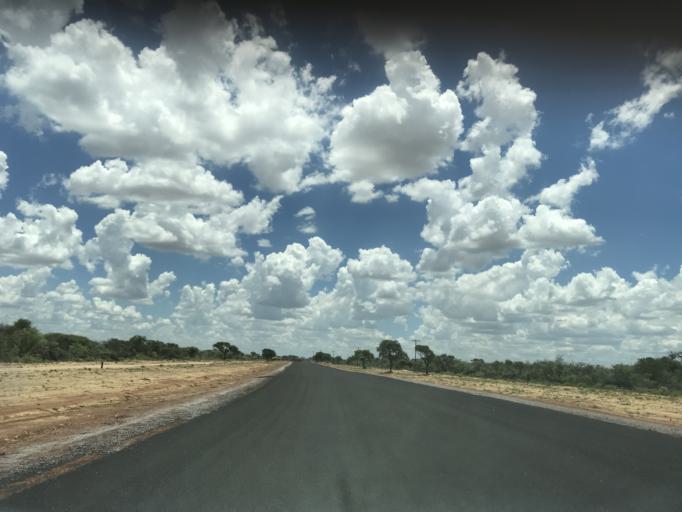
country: BW
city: Mabuli
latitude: -25.7968
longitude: 24.6674
